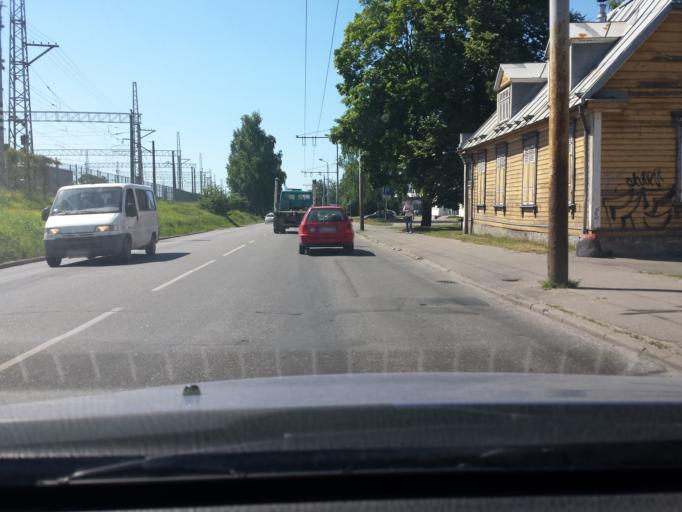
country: LV
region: Riga
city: Riga
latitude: 56.9470
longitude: 24.1400
